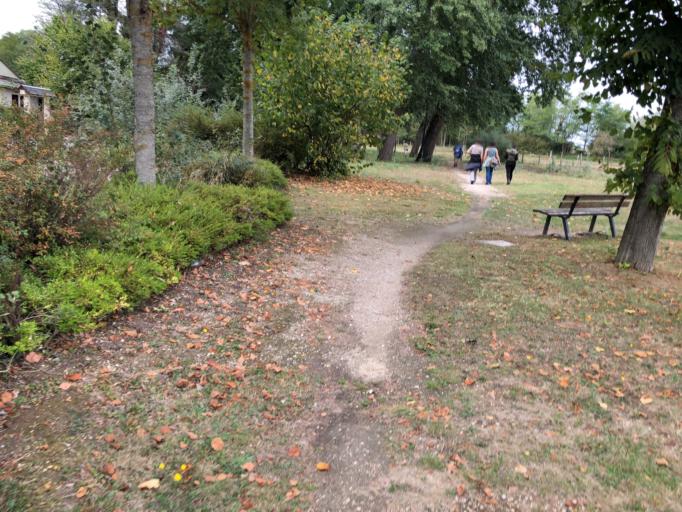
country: FR
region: Centre
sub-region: Departement du Loir-et-Cher
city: Saint-Gervais-la-Foret
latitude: 47.5678
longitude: 1.3442
